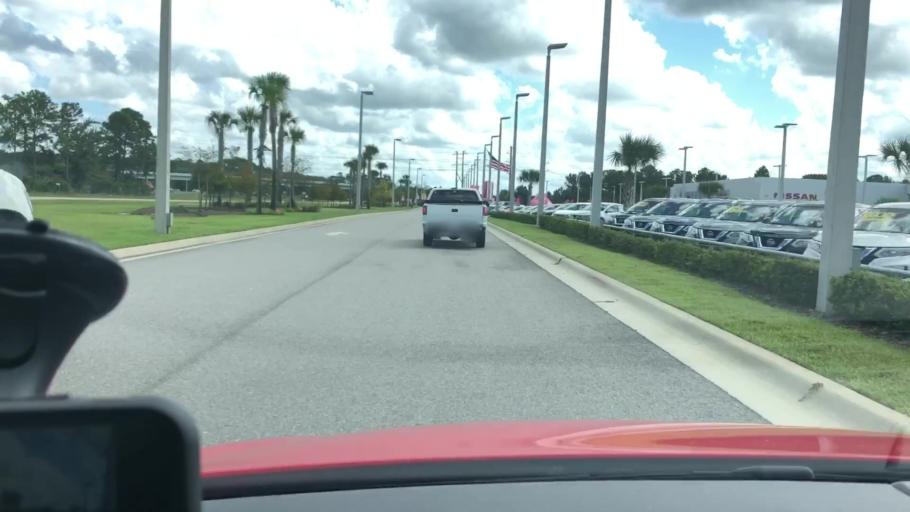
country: US
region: Florida
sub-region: Volusia County
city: Holly Hill
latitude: 29.2011
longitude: -81.0976
